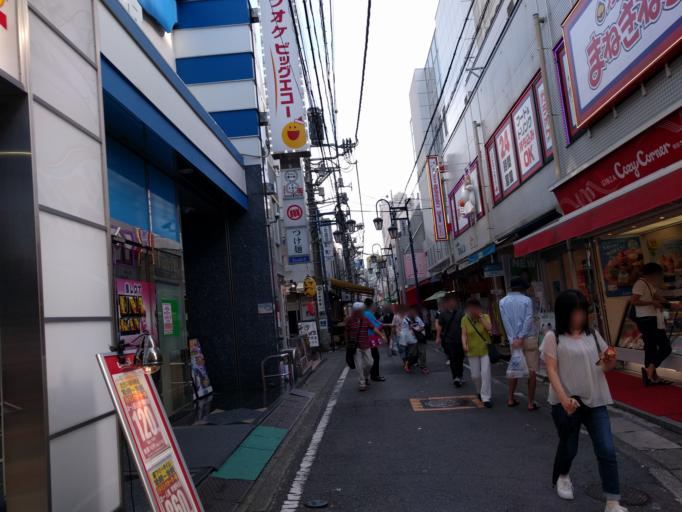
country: JP
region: Kanagawa
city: Kamakura
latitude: 35.3523
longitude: 139.5321
